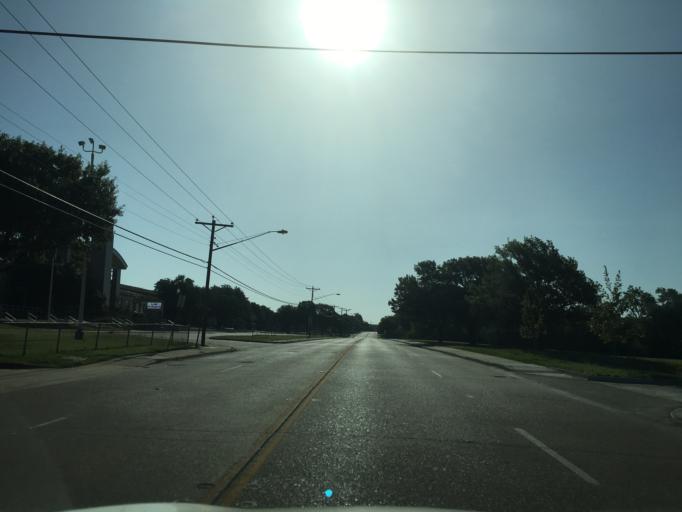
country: US
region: Texas
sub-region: Dallas County
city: Richardson
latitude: 32.8861
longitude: -96.7281
